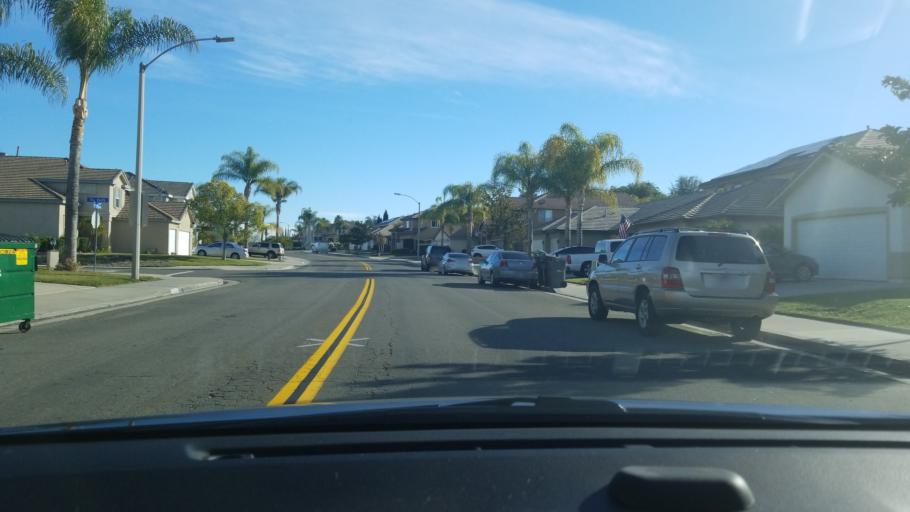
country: US
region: California
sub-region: Riverside County
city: Murrieta
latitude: 33.5710
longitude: -117.1974
